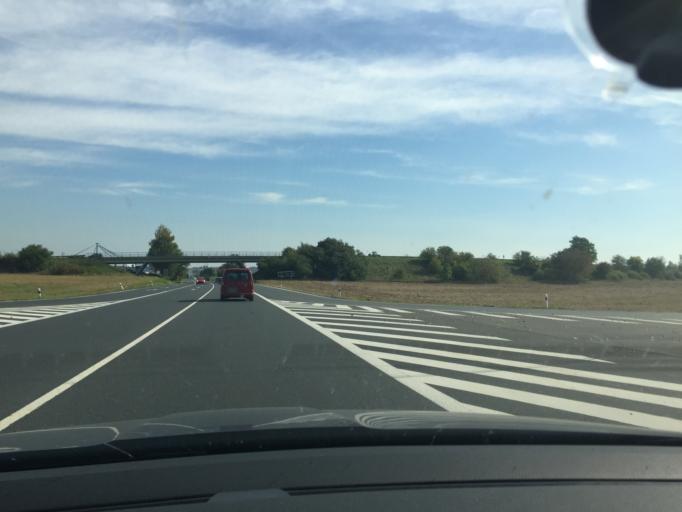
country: CZ
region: Central Bohemia
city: Planany
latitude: 50.0445
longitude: 15.0274
